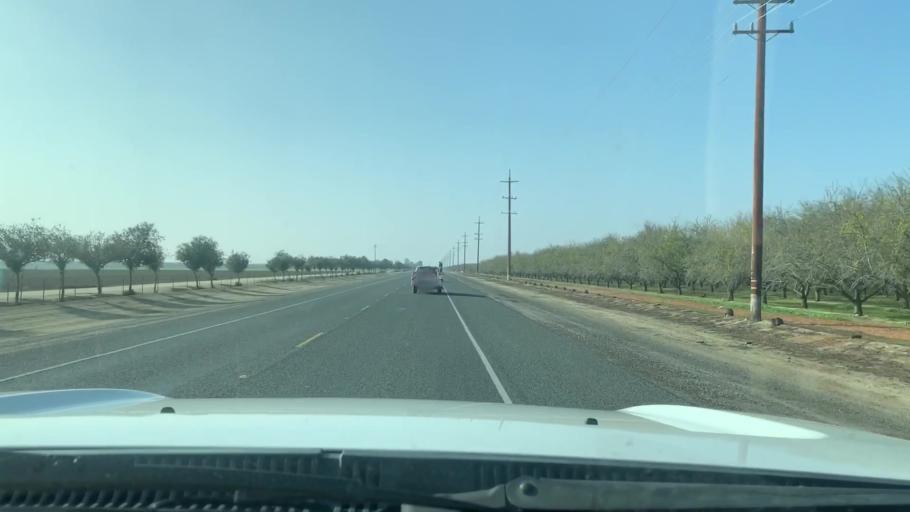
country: US
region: California
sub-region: Kern County
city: Wasco
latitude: 35.6015
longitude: -119.4080
